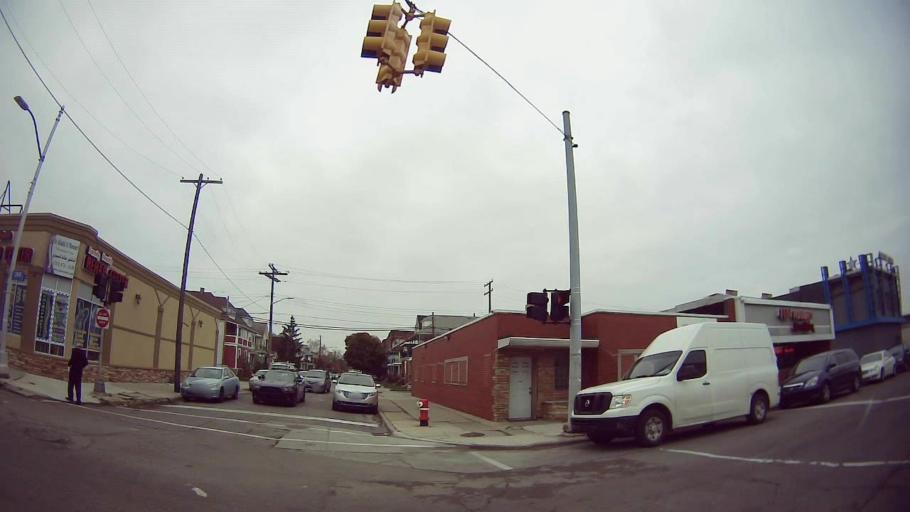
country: US
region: Michigan
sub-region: Wayne County
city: Hamtramck
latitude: 42.3998
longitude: -83.0509
